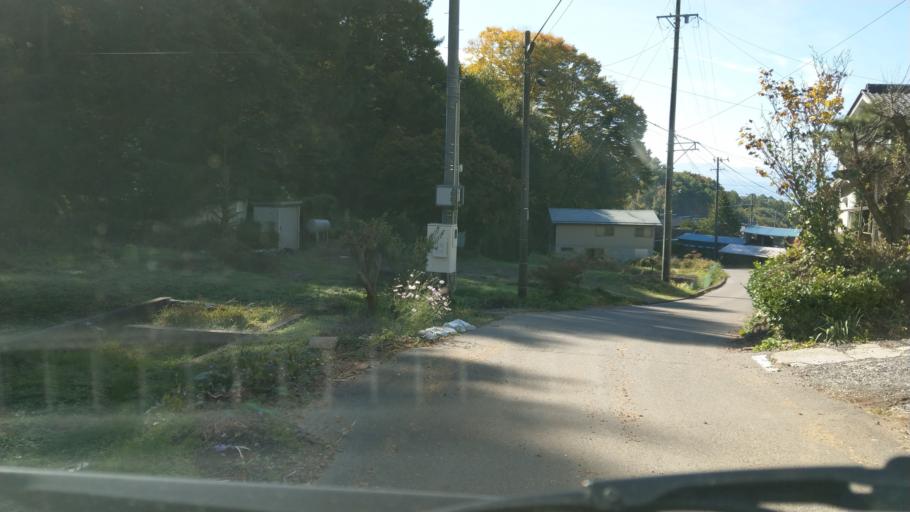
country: JP
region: Nagano
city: Komoro
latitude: 36.3667
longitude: 138.4048
